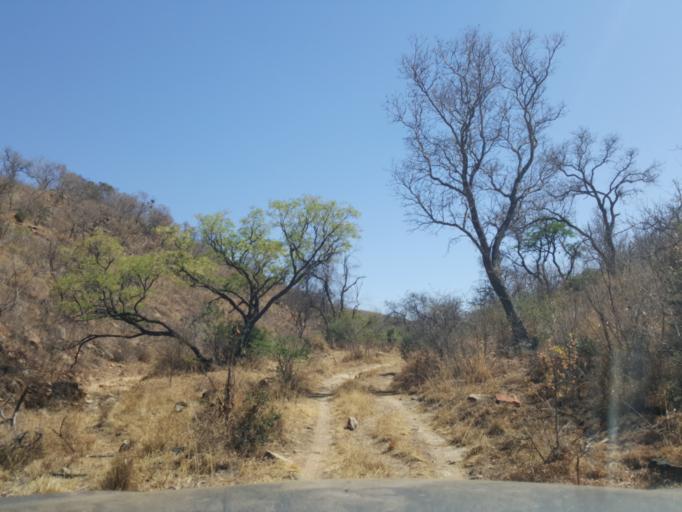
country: BW
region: South East
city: Lobatse
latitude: -25.1511
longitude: 25.6711
